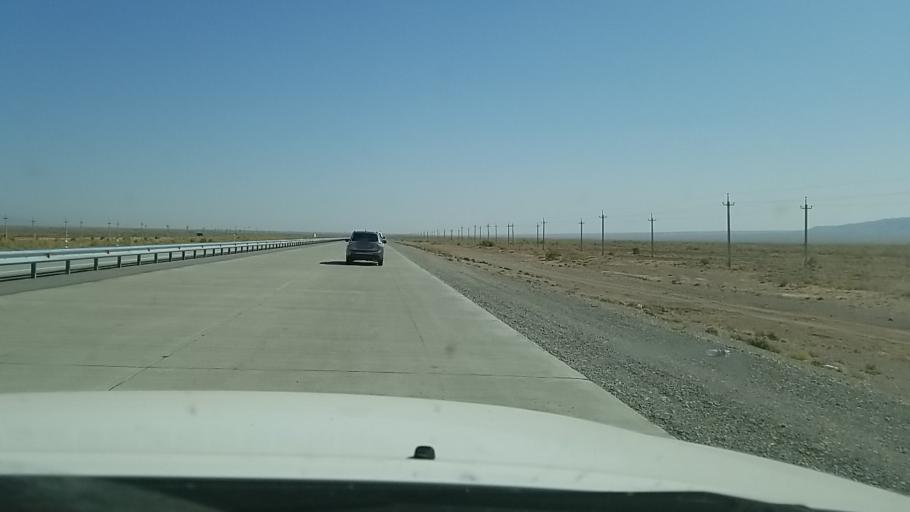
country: KZ
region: Almaty Oblysy
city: Kegen
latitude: 43.7291
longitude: 78.7772
